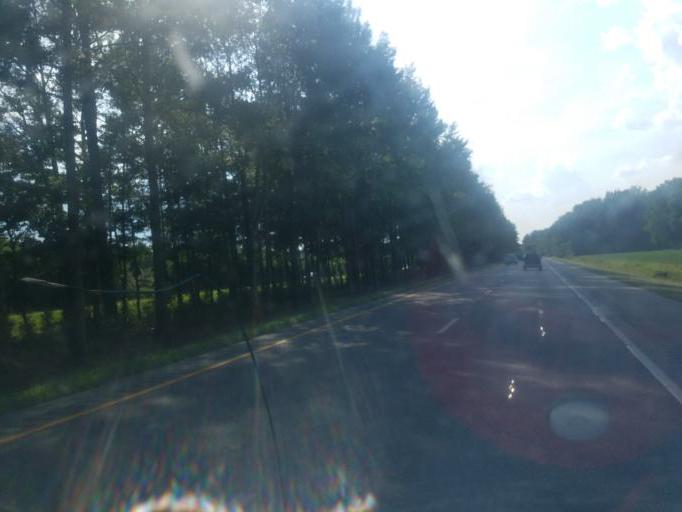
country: US
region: Maryland
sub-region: Worcester County
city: Berlin
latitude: 38.3831
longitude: -75.3001
